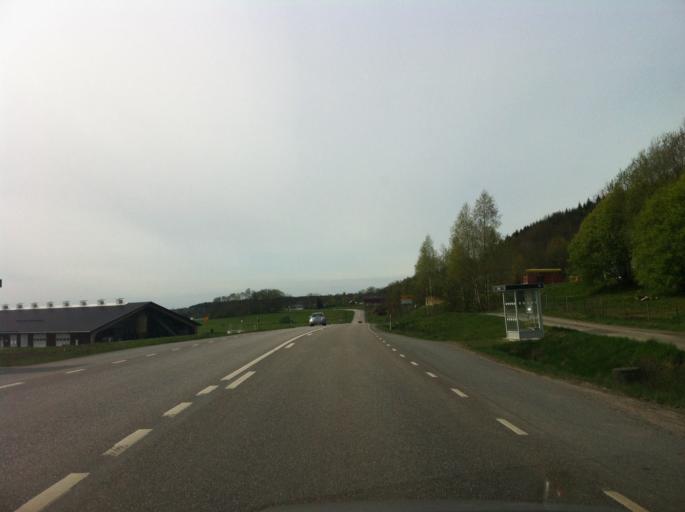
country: SE
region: Vaestra Goetaland
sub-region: Harryda Kommun
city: Ravlanda
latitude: 57.5442
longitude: 12.5342
